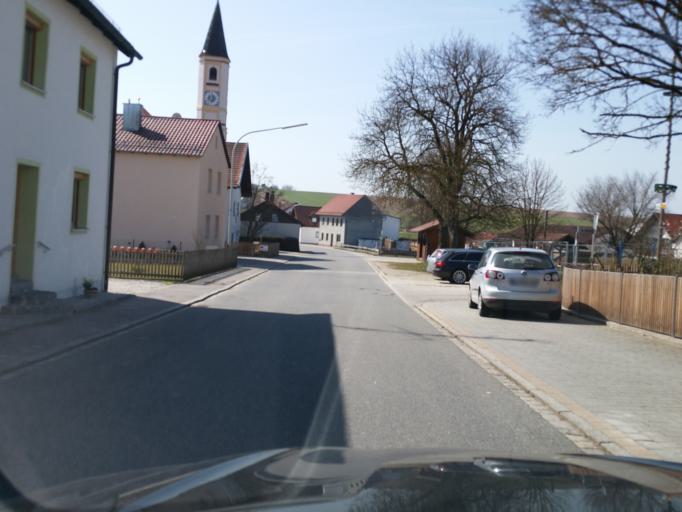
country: DE
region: Bavaria
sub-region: Lower Bavaria
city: Altfraunhofen
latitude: 48.4532
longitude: 12.1469
